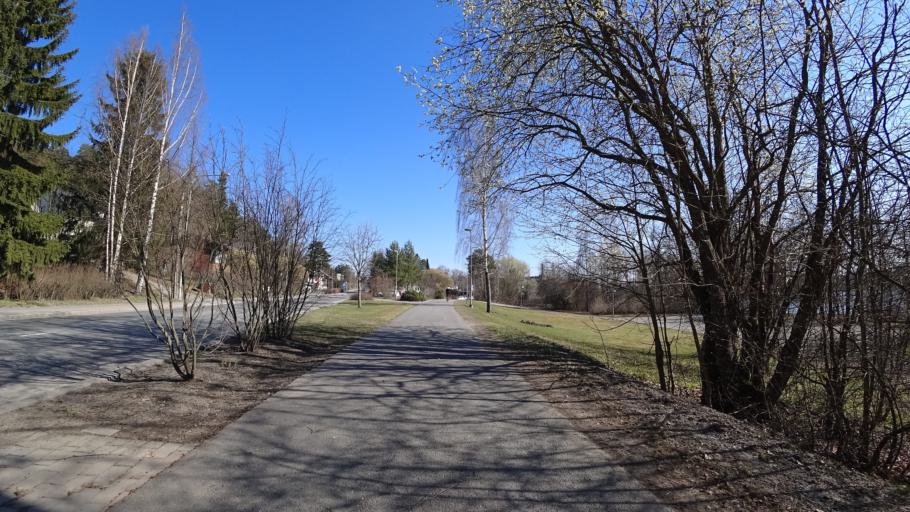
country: FI
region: Pirkanmaa
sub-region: Tampere
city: Pirkkala
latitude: 61.5118
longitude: 23.6596
